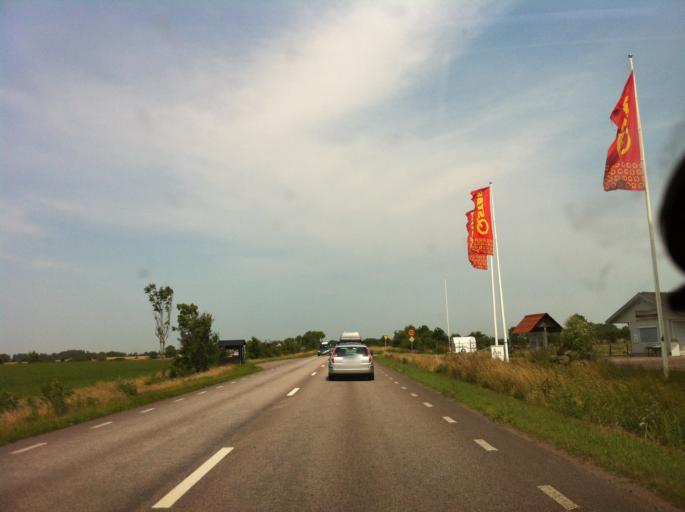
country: SE
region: Kalmar
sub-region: Borgholms Kommun
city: Borgholm
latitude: 56.9574
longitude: 16.7912
